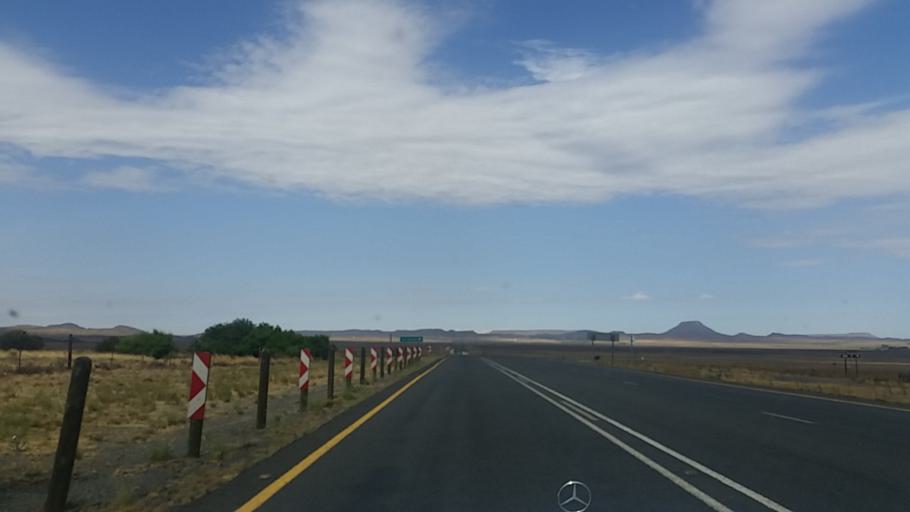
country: ZA
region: Northern Cape
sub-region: Pixley ka Seme District Municipality
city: Colesberg
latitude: -30.6558
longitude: 25.1958
